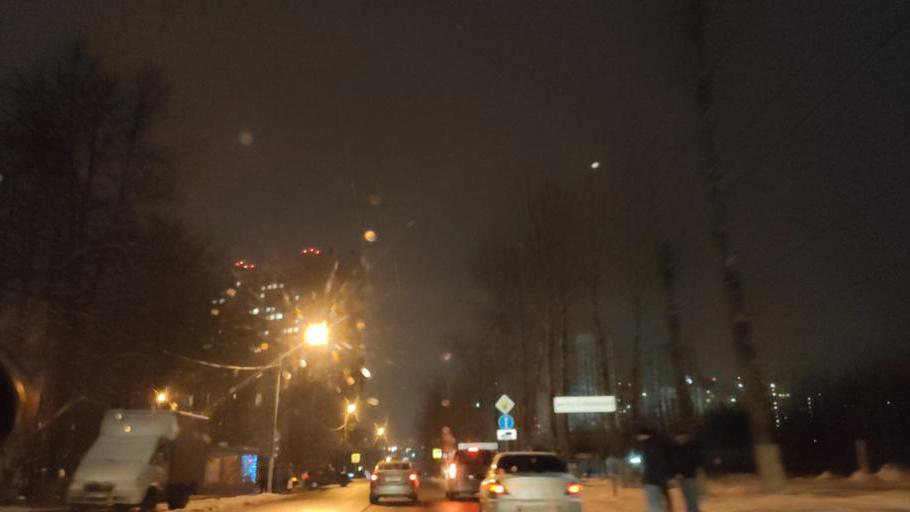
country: RU
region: Moskovskaya
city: Odintsovo
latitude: 55.6839
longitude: 37.2542
